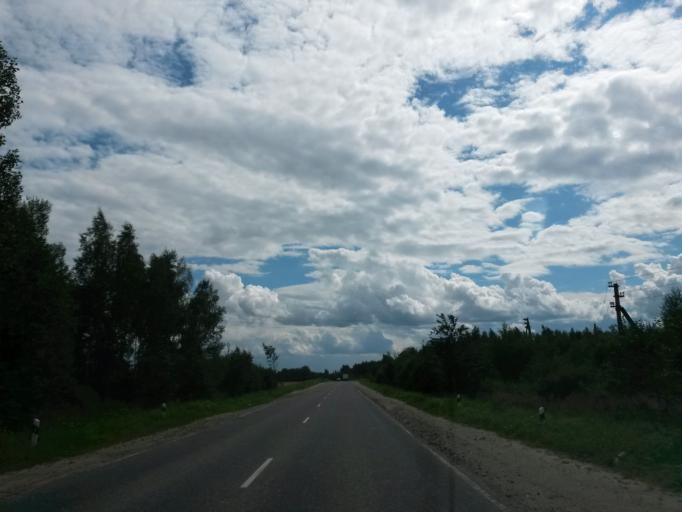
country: RU
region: Ivanovo
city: Novo-Talitsy
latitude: 57.0432
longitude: 40.7411
